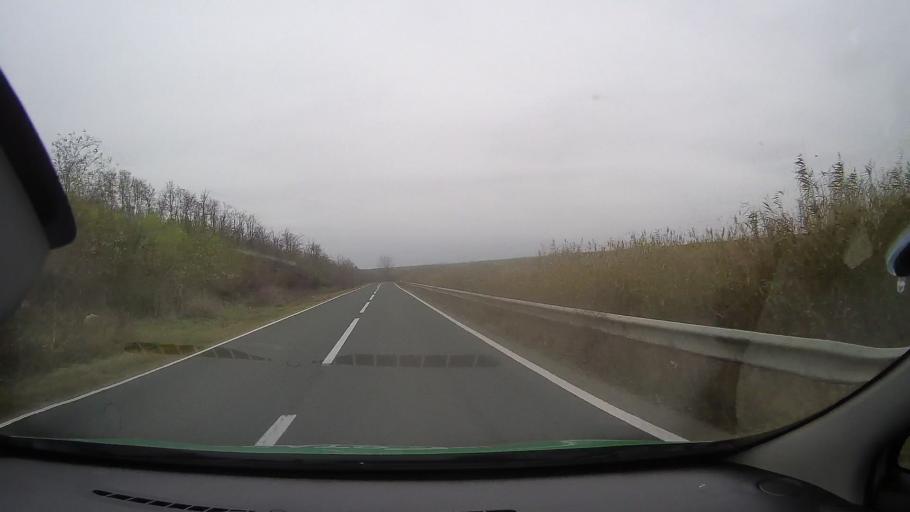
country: RO
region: Constanta
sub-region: Comuna Garliciu
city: Garliciu
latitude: 44.7073
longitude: 28.0609
